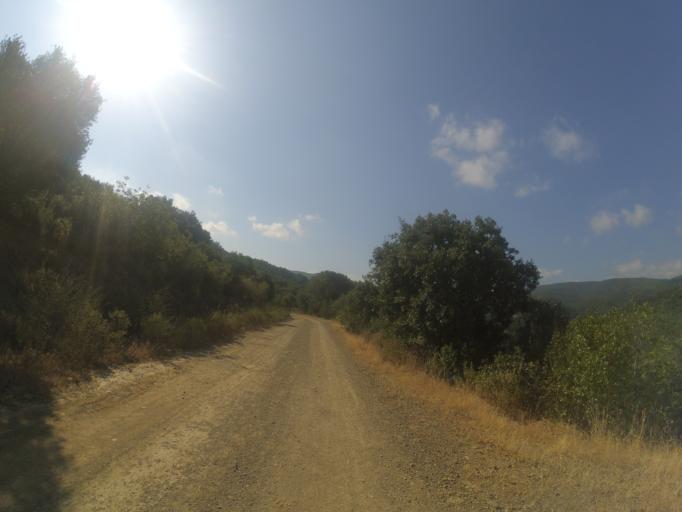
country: FR
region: Languedoc-Roussillon
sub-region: Departement des Pyrenees-Orientales
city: Ille-sur-Tet
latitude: 42.6506
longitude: 2.6255
